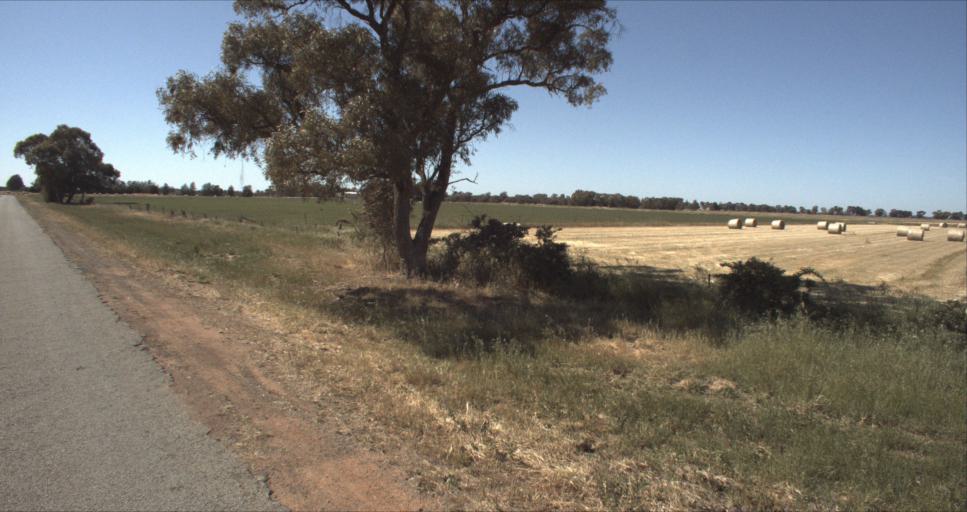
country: AU
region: New South Wales
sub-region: Leeton
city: Leeton
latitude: -34.5334
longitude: 146.3213
